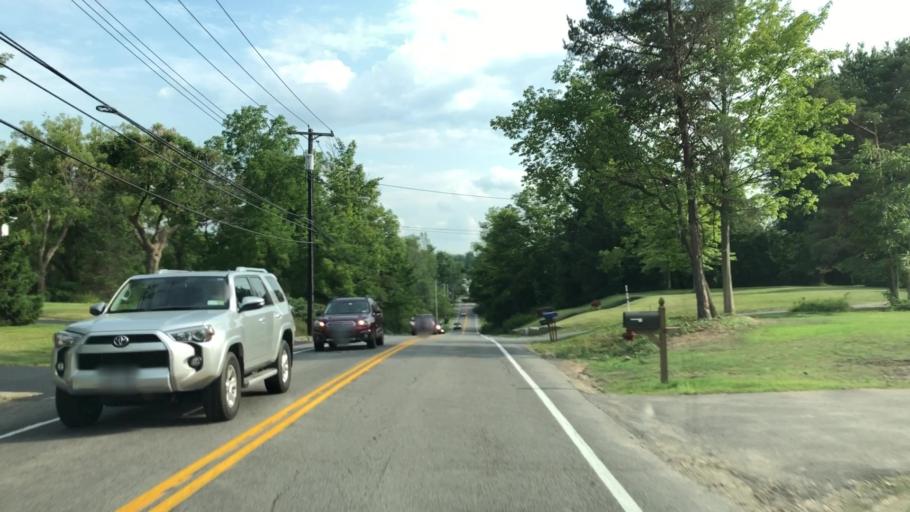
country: US
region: New York
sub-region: Erie County
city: Elma Center
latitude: 42.8542
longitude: -78.6403
